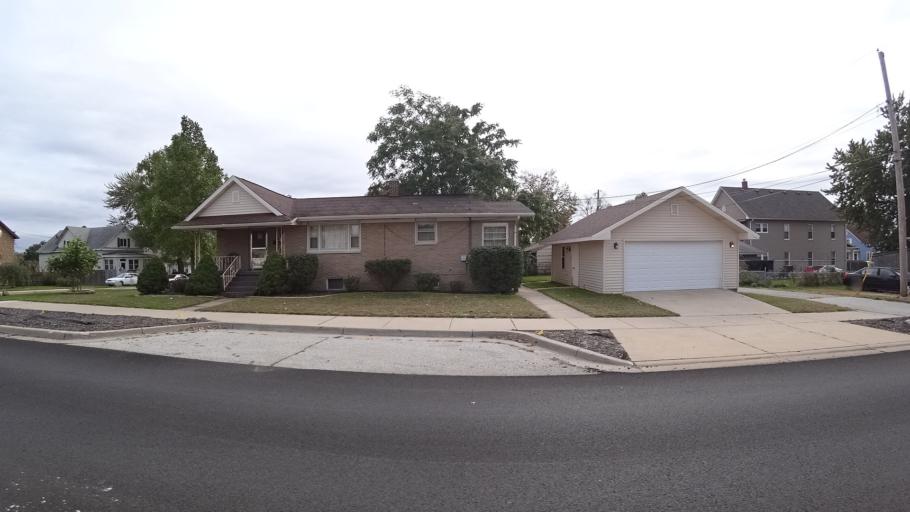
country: US
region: Indiana
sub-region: LaPorte County
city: Michigan City
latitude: 41.7047
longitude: -86.9032
